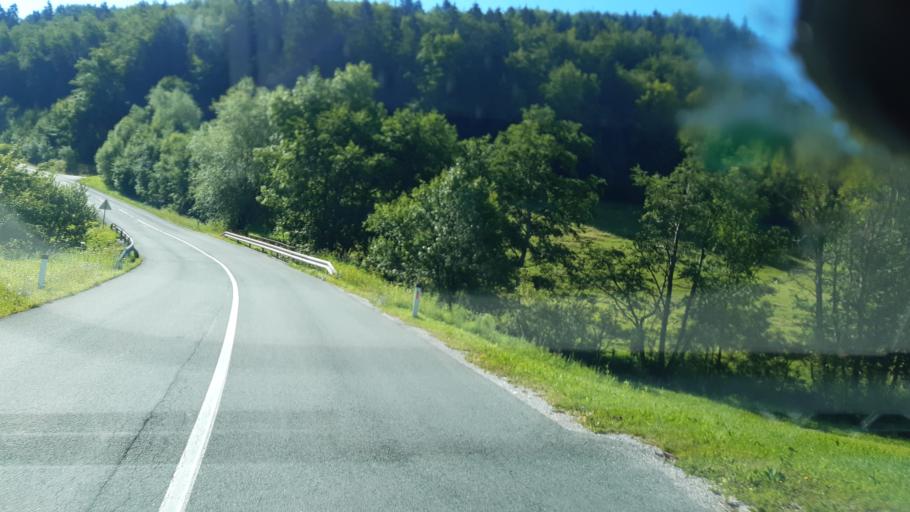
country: SI
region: Gornji Grad
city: Gornji Grad
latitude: 46.2167
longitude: 14.7932
